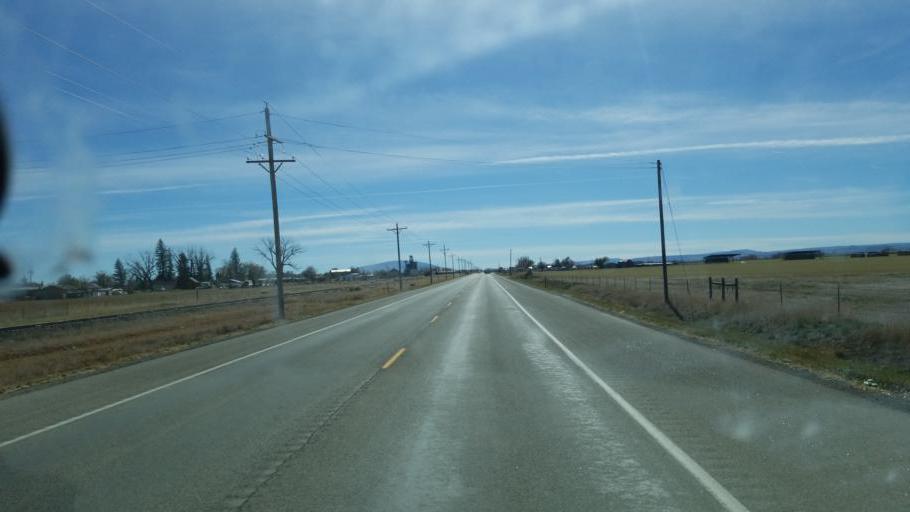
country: US
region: Colorado
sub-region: Conejos County
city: Conejos
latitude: 37.1799
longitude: -105.9863
